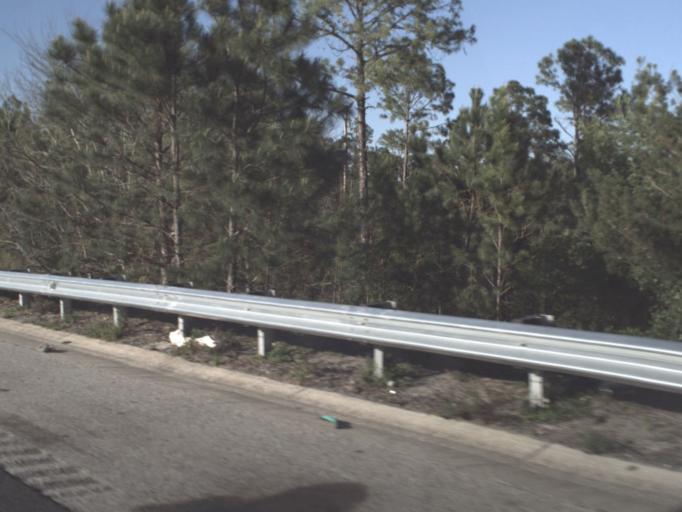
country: US
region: Florida
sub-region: Flagler County
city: Flagler Beach
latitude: 29.4987
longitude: -81.1923
